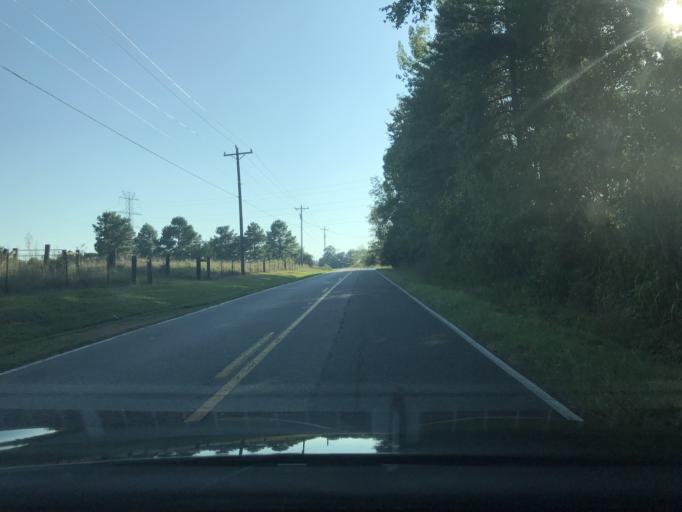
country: US
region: South Carolina
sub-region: Spartanburg County
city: Mayo
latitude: 35.1356
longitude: -81.7627
